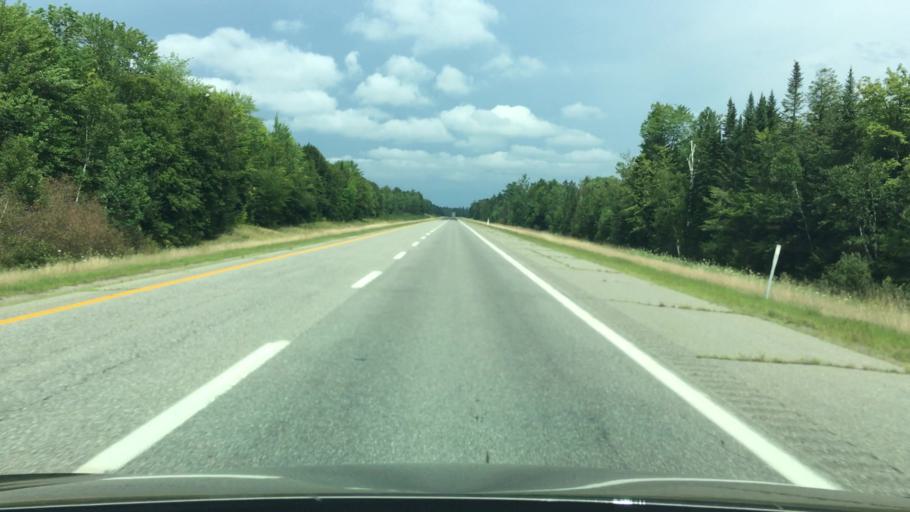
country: US
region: Maine
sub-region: Penobscot County
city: Howland
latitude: 45.2972
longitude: -68.6627
